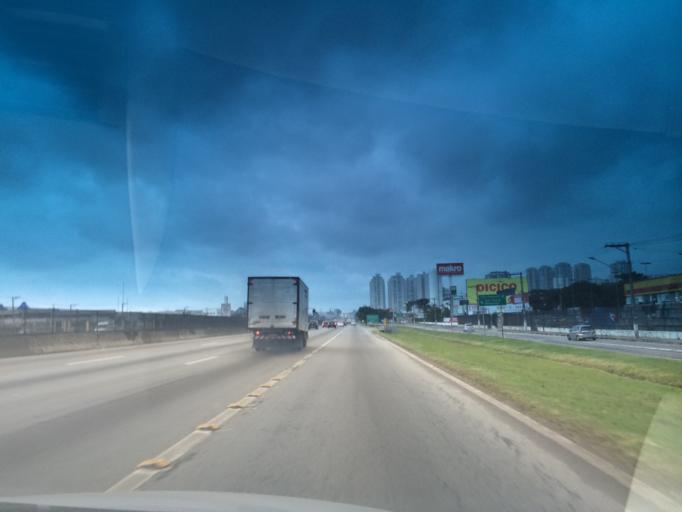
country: BR
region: Sao Paulo
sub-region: Guarulhos
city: Guarulhos
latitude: -23.4783
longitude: -46.5298
